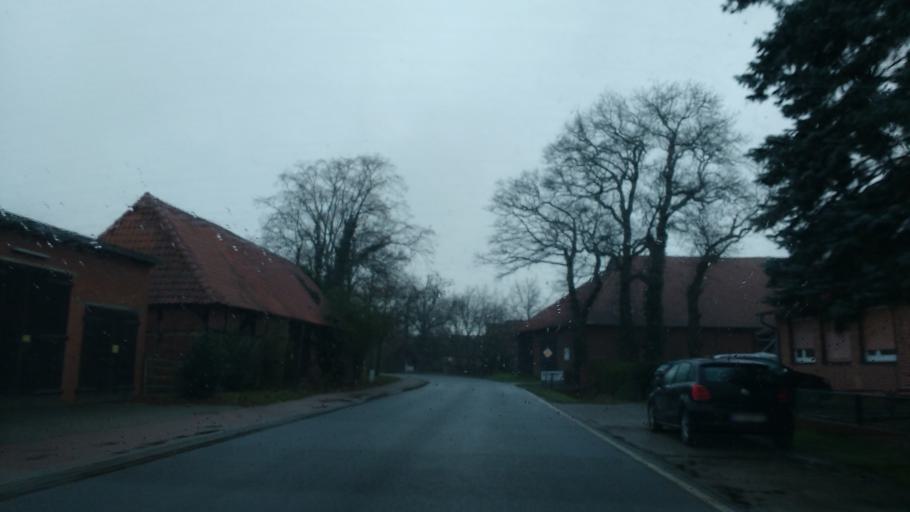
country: DE
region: Lower Saxony
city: Gilten
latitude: 52.6644
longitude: 9.5738
